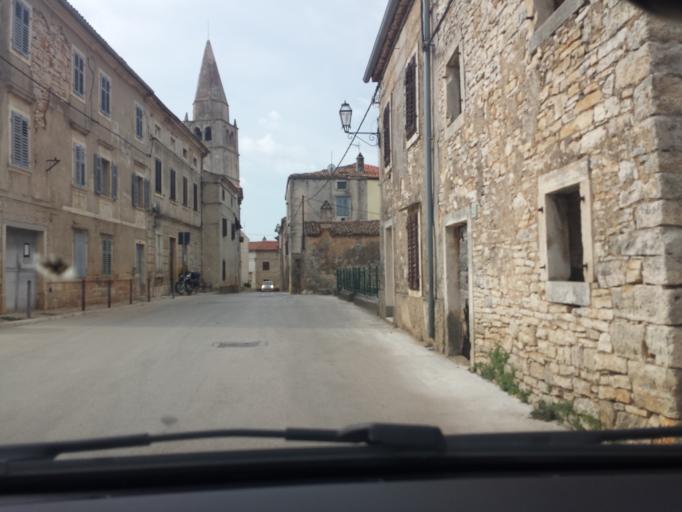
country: HR
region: Istarska
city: Galizana
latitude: 44.9346
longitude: 13.8702
